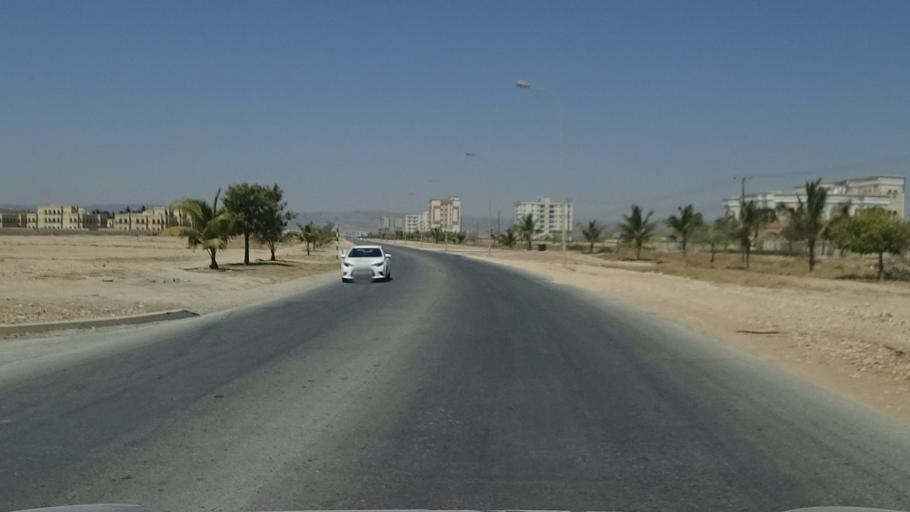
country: OM
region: Zufar
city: Salalah
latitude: 17.0398
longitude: 54.1716
